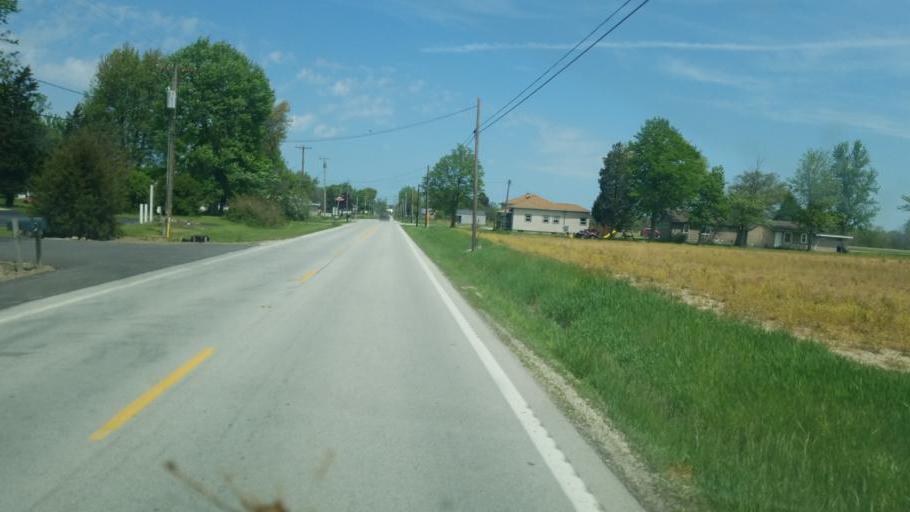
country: US
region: Ohio
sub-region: Ottawa County
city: Oak Harbor
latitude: 41.4959
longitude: -83.1452
